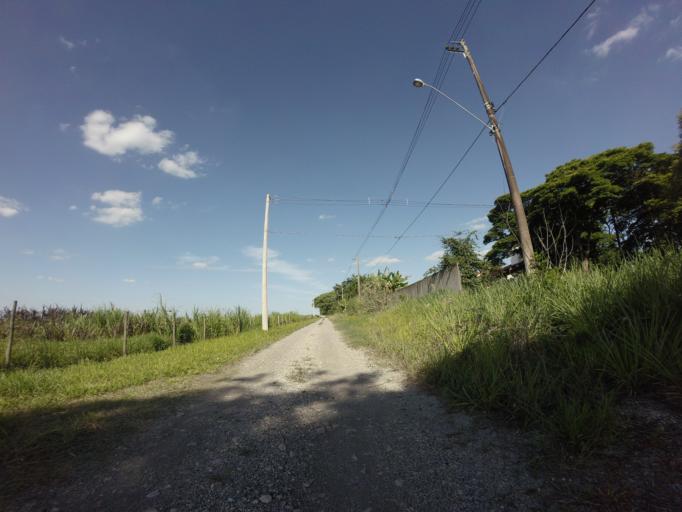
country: BR
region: Sao Paulo
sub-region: Piracicaba
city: Piracicaba
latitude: -22.7496
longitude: -47.5897
